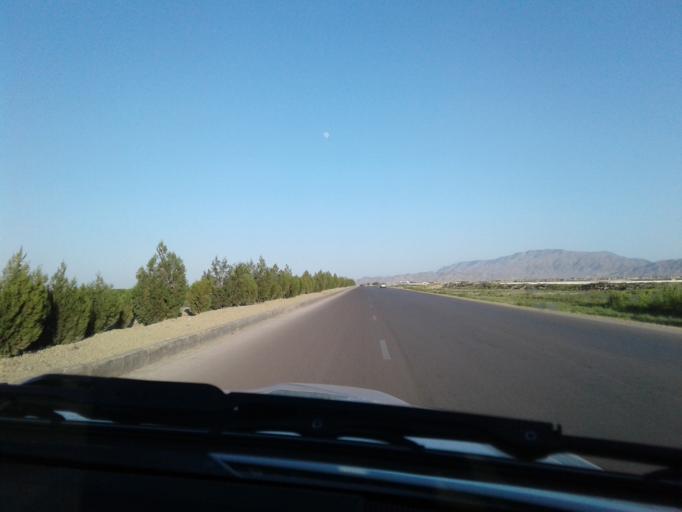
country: TM
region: Ahal
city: Baharly
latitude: 38.3373
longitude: 57.5690
